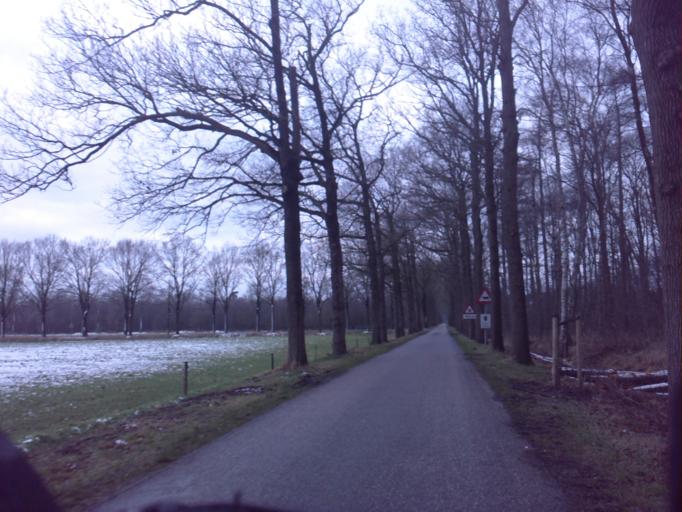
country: NL
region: Utrecht
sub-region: Gemeente Leusden
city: Leusden
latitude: 52.1061
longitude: 5.4853
